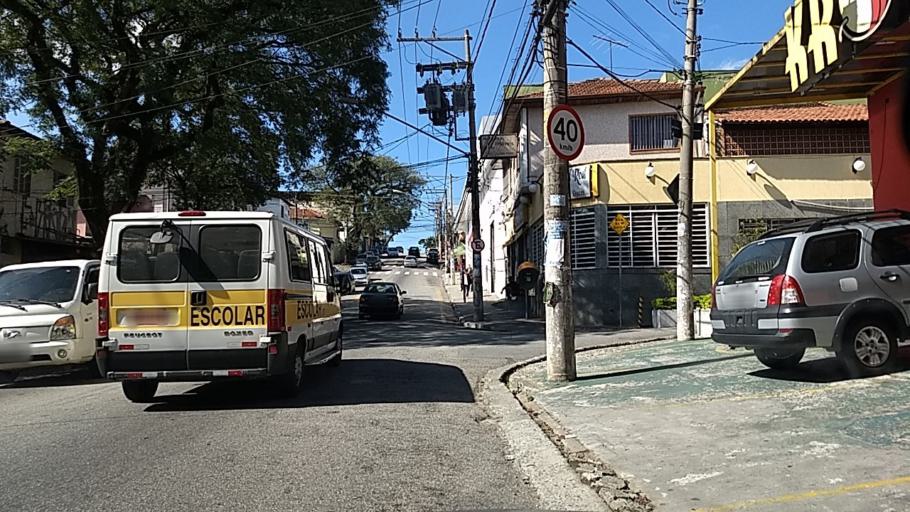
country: BR
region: Sao Paulo
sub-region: Guarulhos
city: Guarulhos
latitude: -23.4825
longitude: -46.5889
